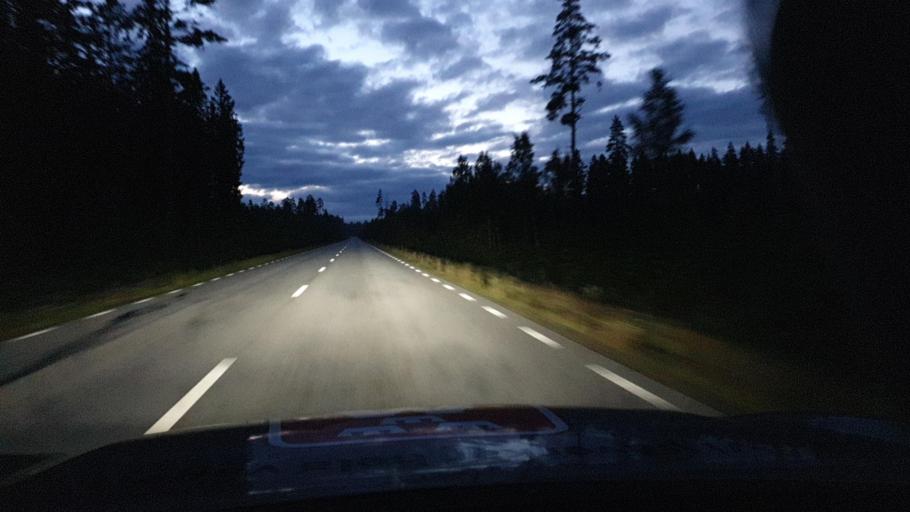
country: SE
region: OErebro
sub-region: Karlskoga Kommun
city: Karlskoga
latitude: 59.4048
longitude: 14.5138
